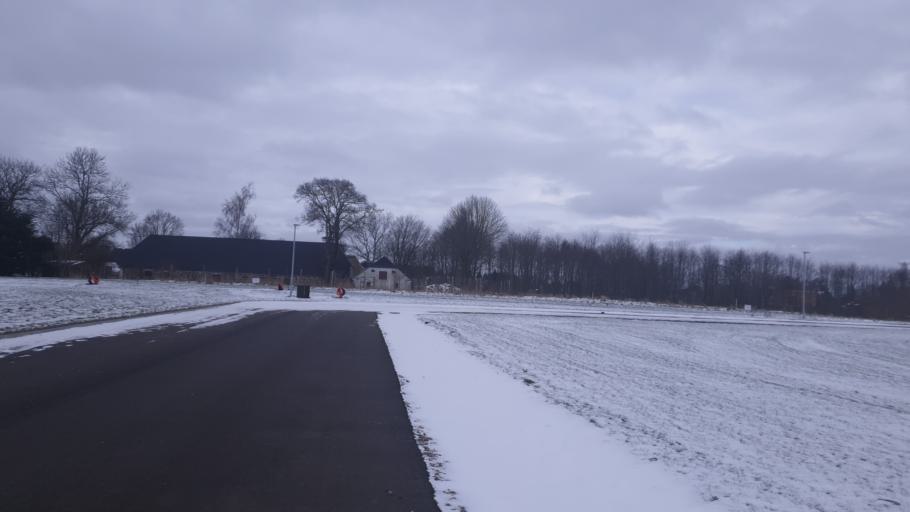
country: DK
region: Central Jutland
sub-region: Hedensted Kommune
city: Hedensted
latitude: 55.8020
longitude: 9.7071
